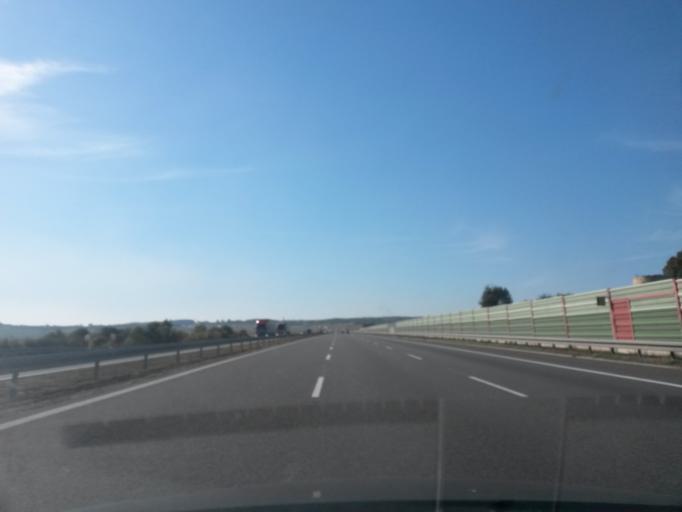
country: PL
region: Opole Voivodeship
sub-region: Powiat strzelecki
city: Lesnica
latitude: 50.4666
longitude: 18.1952
